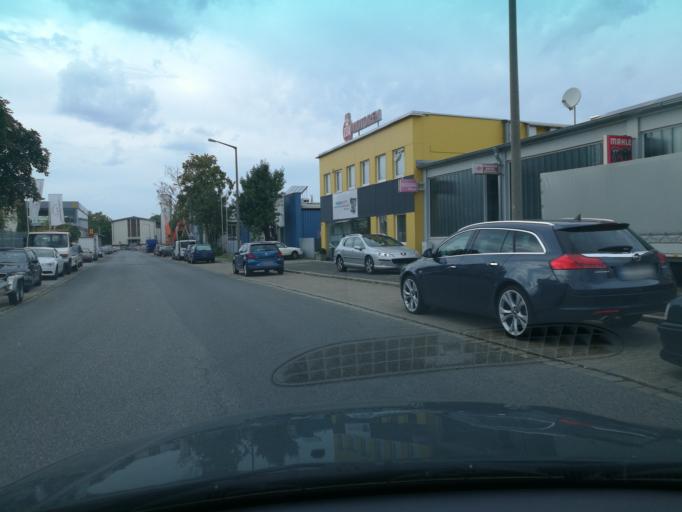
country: DE
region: Bavaria
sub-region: Regierungsbezirk Mittelfranken
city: Nuernberg
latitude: 49.4716
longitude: 11.0747
